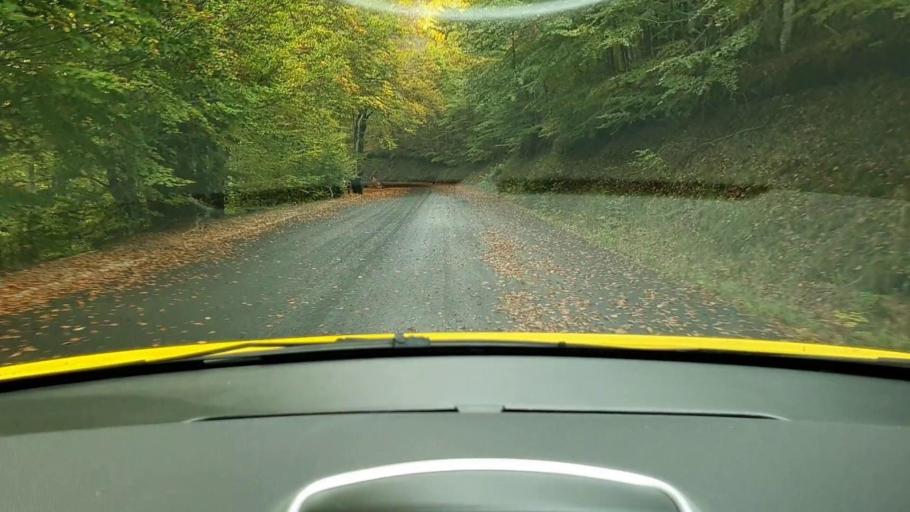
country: FR
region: Languedoc-Roussillon
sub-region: Departement du Gard
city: Valleraugue
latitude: 44.0785
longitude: 3.5339
